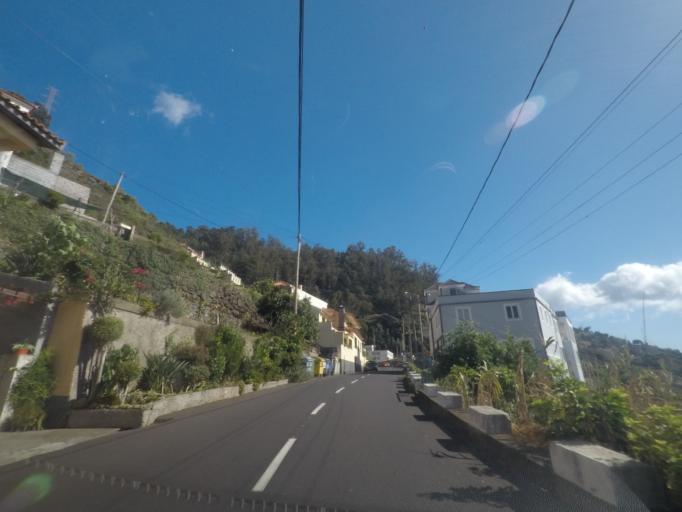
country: PT
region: Madeira
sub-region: Ribeira Brava
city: Campanario
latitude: 32.6708
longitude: -17.0213
